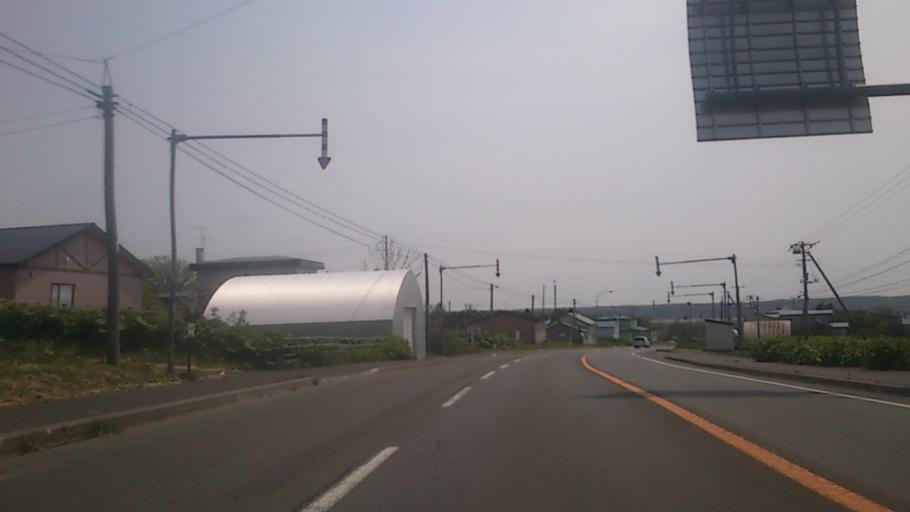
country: JP
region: Hokkaido
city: Nemuro
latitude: 43.2797
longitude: 145.5062
